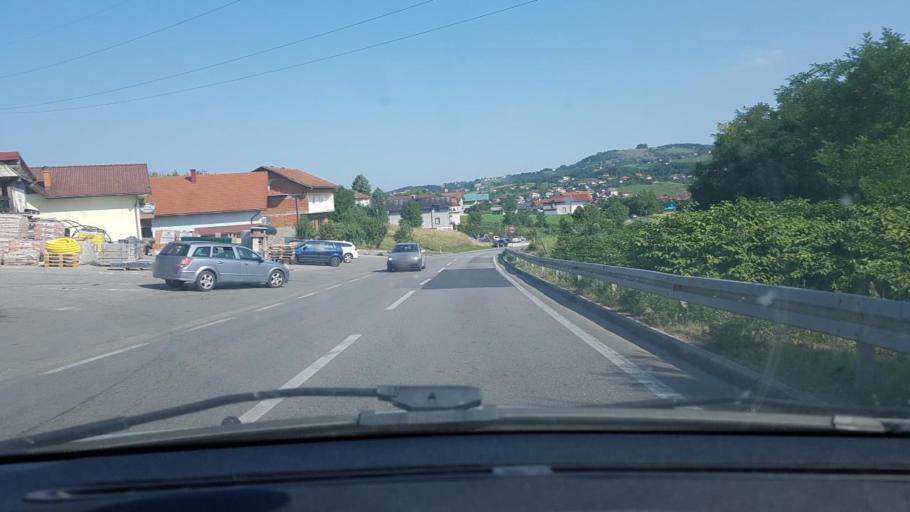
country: BA
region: Federation of Bosnia and Herzegovina
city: Cazin
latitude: 44.9605
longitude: 15.9281
